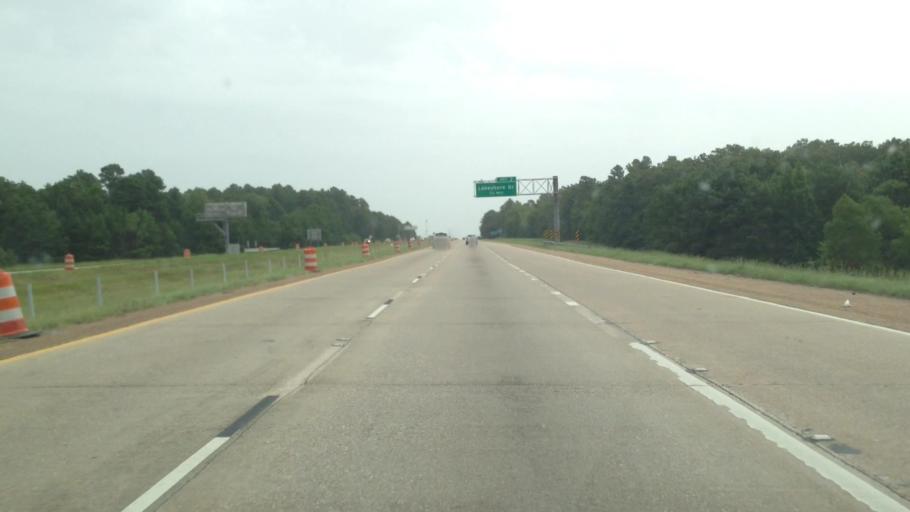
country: US
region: Louisiana
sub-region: Caddo Parish
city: Shreveport
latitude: 32.4762
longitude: -93.8349
